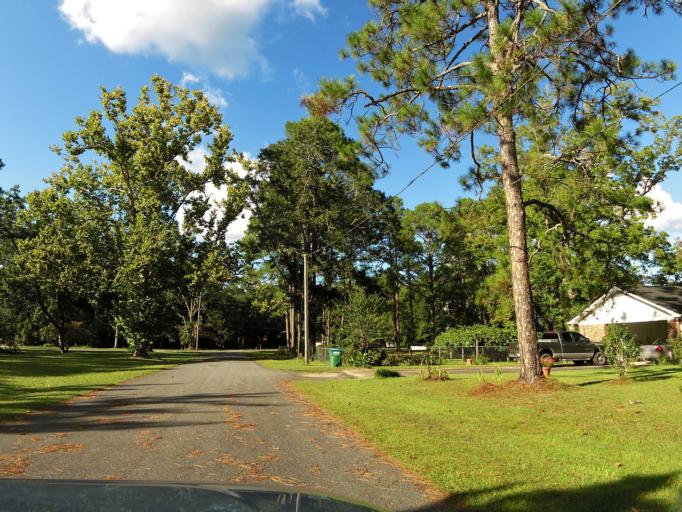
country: US
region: Florida
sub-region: Wakulla County
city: Crawfordville
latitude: 30.0609
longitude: -84.4950
